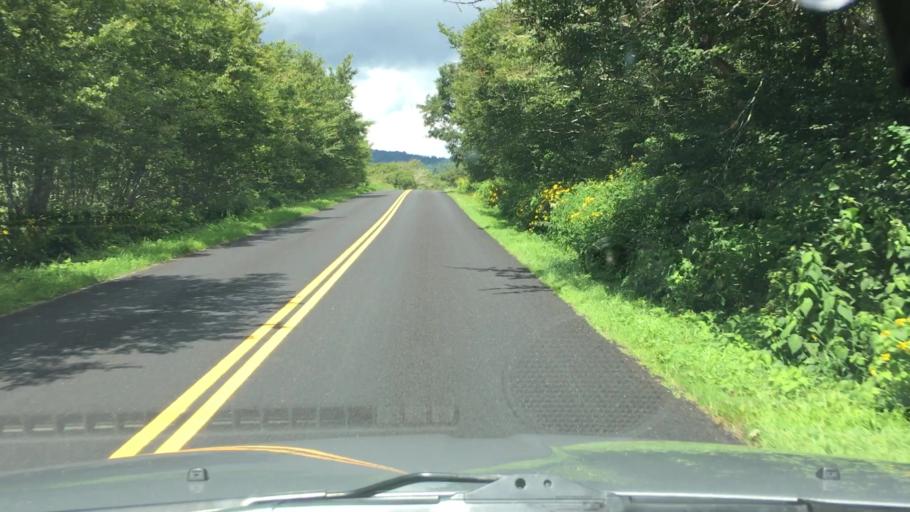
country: US
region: North Carolina
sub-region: Buncombe County
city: Black Mountain
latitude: 35.7330
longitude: -82.3448
